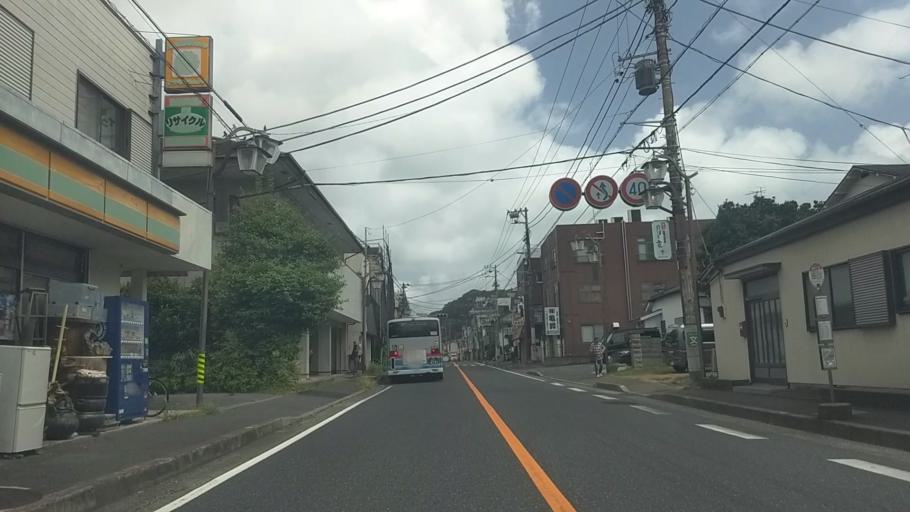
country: JP
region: Kanagawa
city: Yokosuka
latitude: 35.2579
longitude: 139.6668
